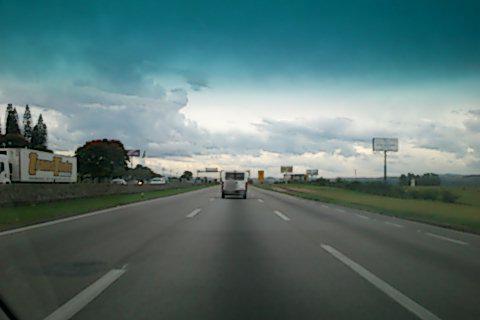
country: BR
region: Sao Paulo
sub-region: Jacarei
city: Jacarei
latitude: -23.2510
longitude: -45.9369
